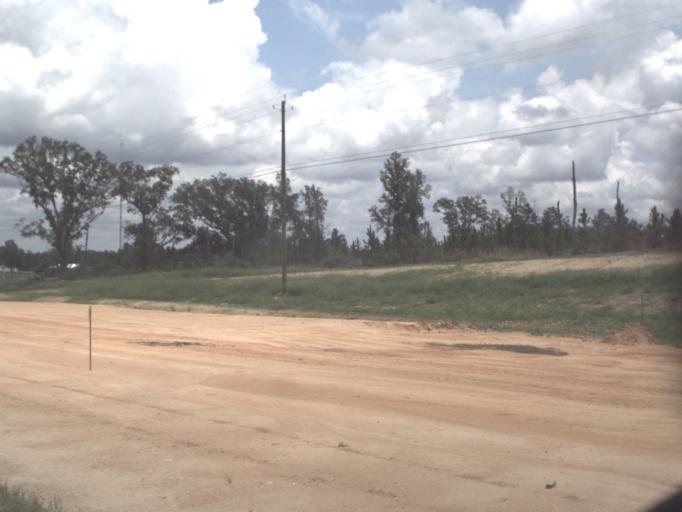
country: US
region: Florida
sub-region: Holmes County
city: Bonifay
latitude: 30.6962
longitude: -85.6865
